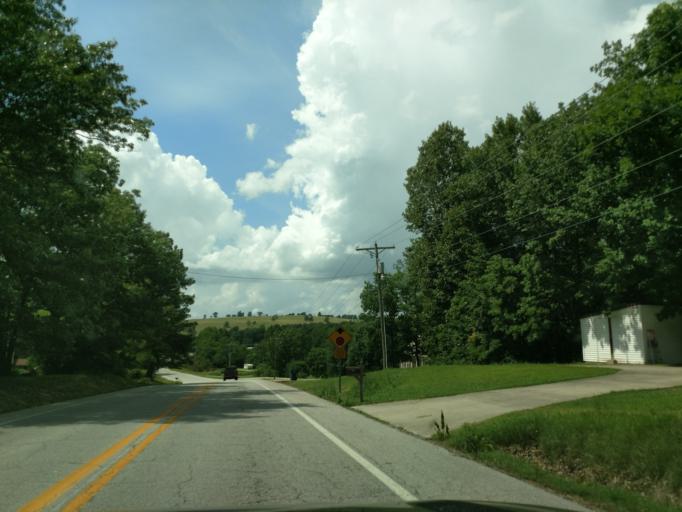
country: US
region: Arkansas
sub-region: Boone County
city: Harrison
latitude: 36.2910
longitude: -93.2396
